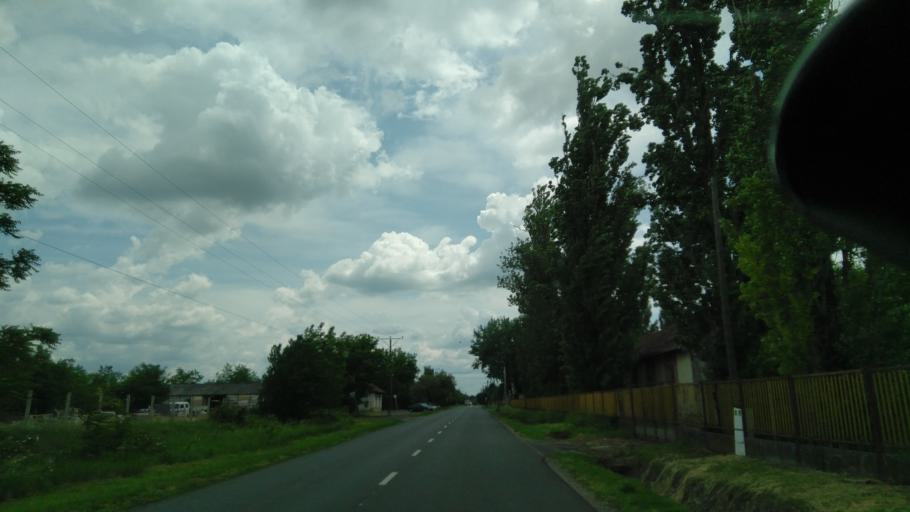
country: HU
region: Bekes
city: Totkomlos
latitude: 46.4259
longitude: 20.7315
